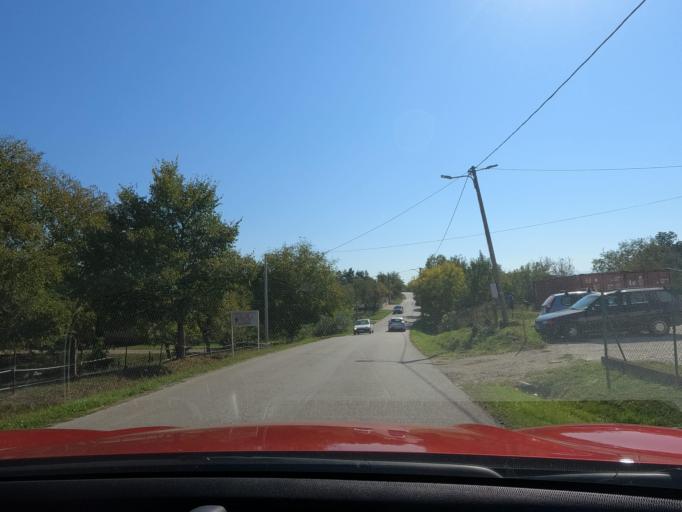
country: RS
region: Central Serbia
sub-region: Raski Okrug
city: Kraljevo
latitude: 43.7611
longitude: 20.6785
